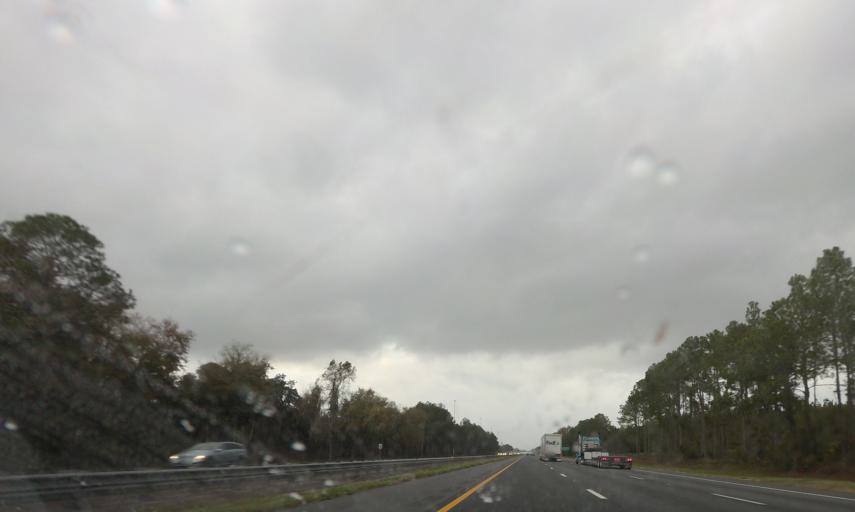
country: US
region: Florida
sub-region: Hamilton County
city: Jasper
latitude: 30.4434
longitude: -82.9242
